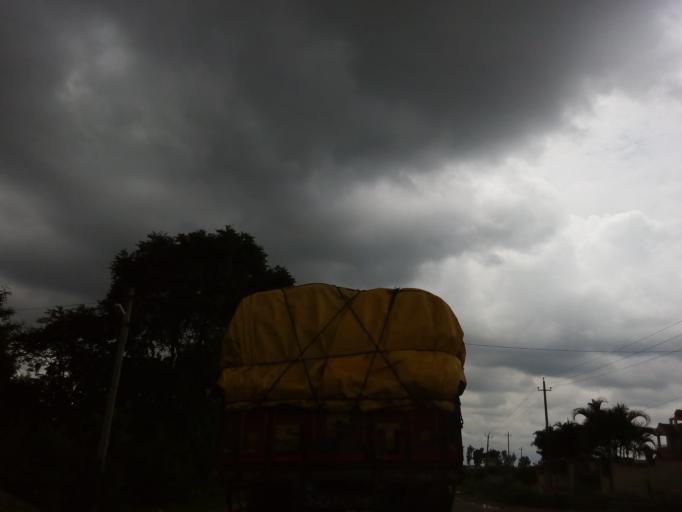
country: IN
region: Karnataka
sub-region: Hassan
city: Belur
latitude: 13.1632
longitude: 75.8847
